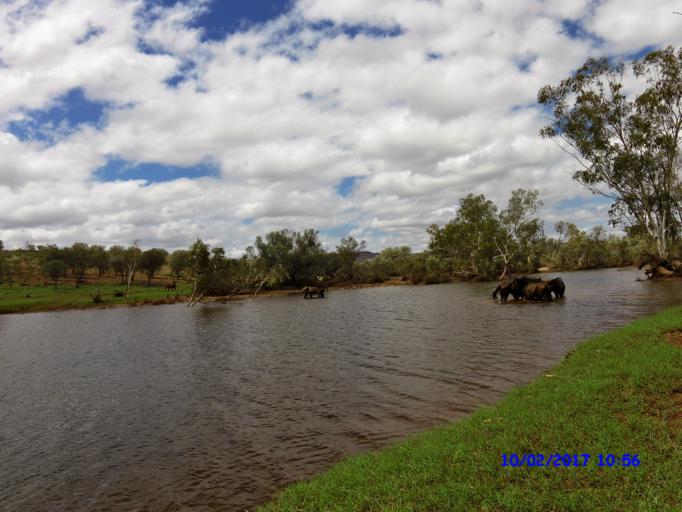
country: AU
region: Western Australia
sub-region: Ashburton
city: Tom Price
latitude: -23.1071
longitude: 117.8700
